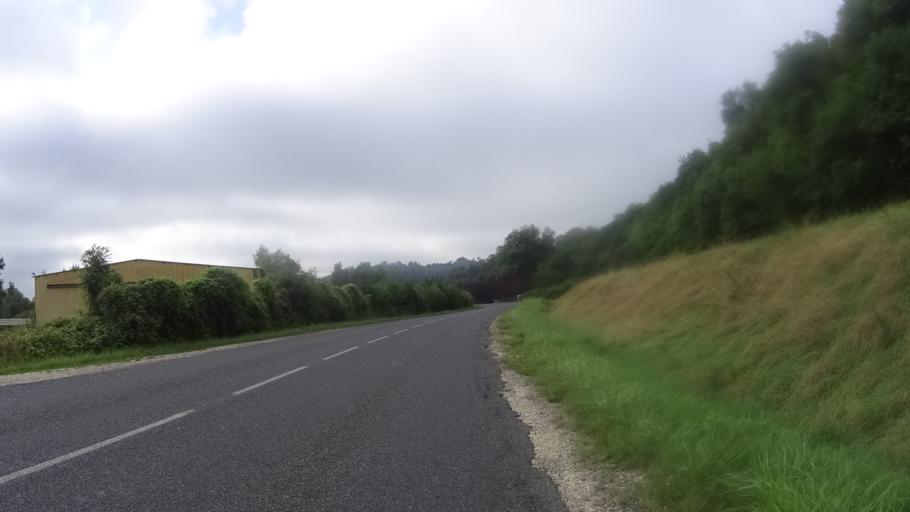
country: FR
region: Lorraine
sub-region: Departement de la Meuse
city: Fains-Veel
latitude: 48.7995
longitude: 5.1121
